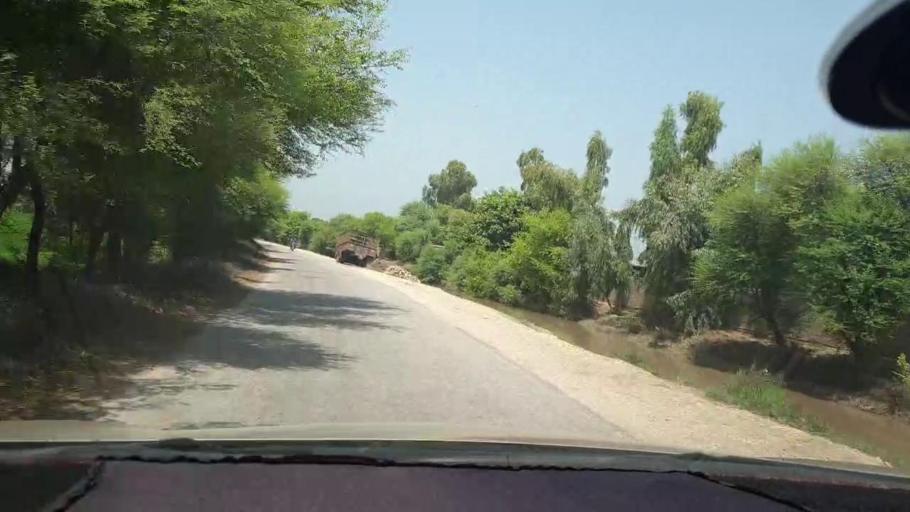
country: PK
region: Sindh
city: Kambar
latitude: 27.6482
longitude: 67.9687
